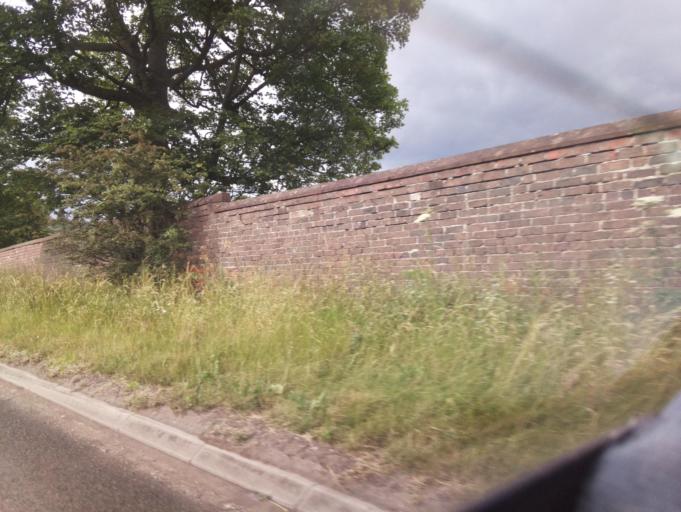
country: GB
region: England
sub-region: Dudley
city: Kingswinford
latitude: 52.5268
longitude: -2.1784
